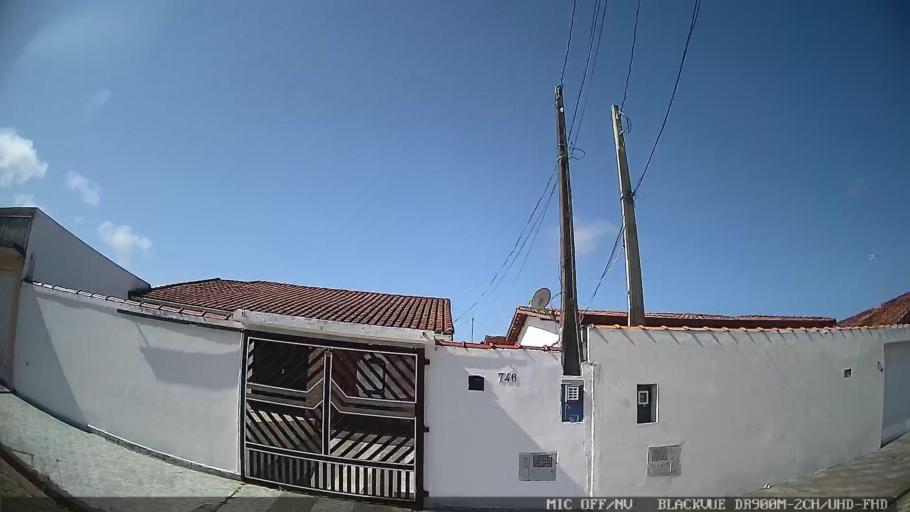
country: BR
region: Sao Paulo
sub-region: Peruibe
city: Peruibe
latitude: -24.3062
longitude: -46.9874
